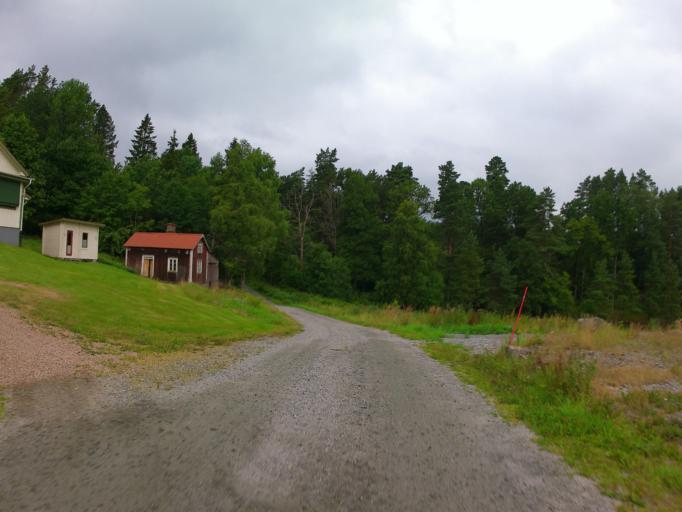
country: SE
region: Vaestra Goetaland
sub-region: Vargarda Kommun
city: Jonstorp
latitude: 58.0327
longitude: 12.6239
